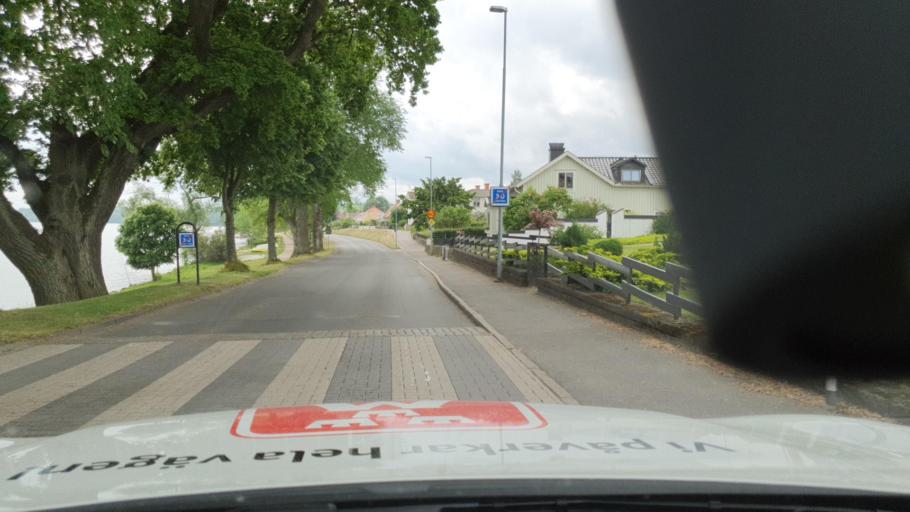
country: SE
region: Vaestra Goetaland
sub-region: Hjo Kommun
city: Hjo
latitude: 58.2990
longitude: 14.2864
